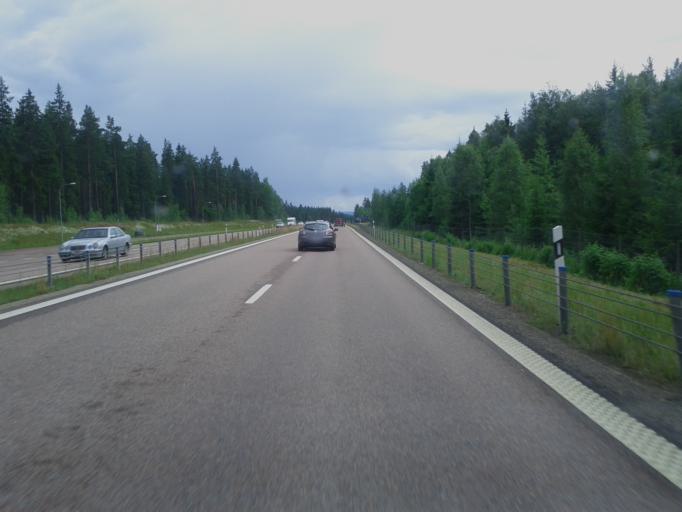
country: SE
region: Dalarna
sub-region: Borlange Kommun
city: Ornas
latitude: 60.5286
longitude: 15.5528
